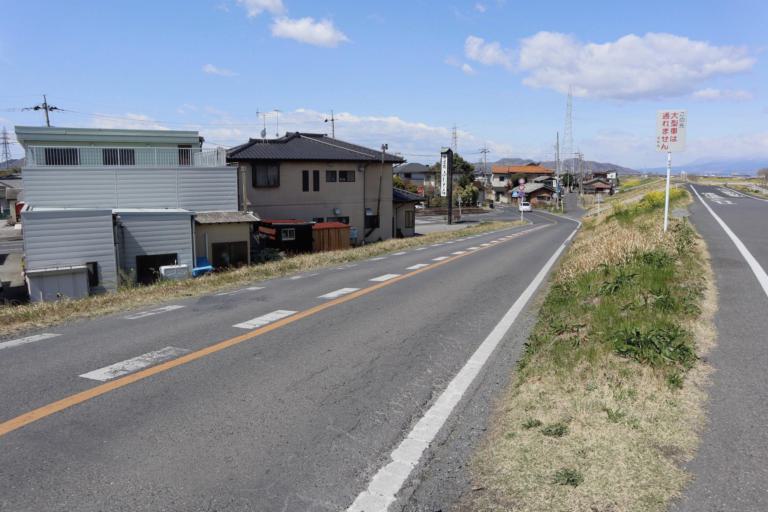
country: JP
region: Tochigi
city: Ashikaga
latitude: 36.3324
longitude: 139.4271
